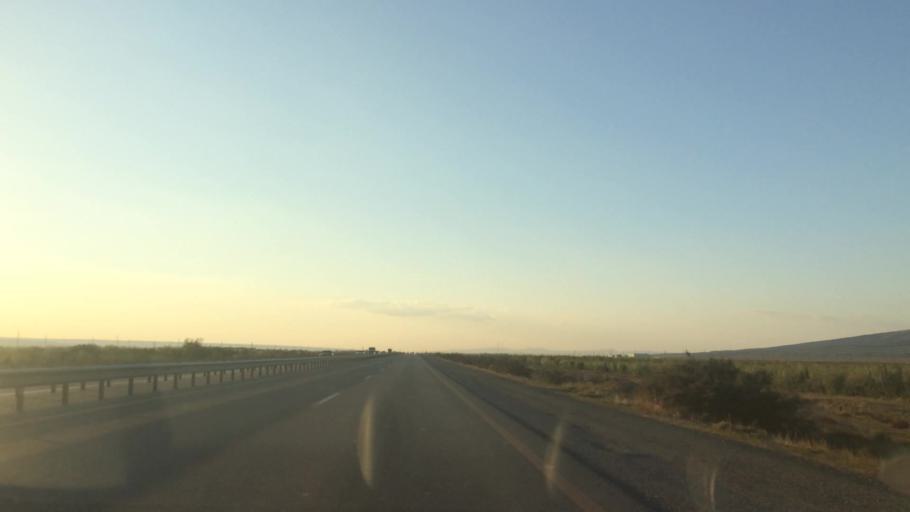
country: AZ
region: Baki
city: Qobustan
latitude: 39.9553
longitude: 49.3094
